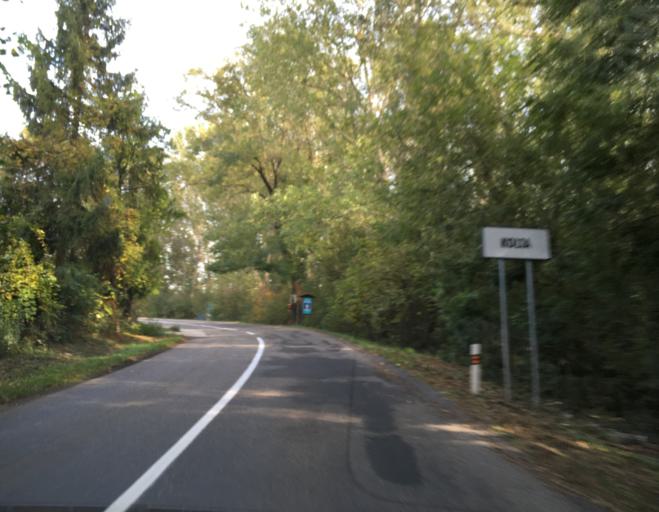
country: SK
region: Nitriansky
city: Svodin
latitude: 48.0054
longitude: 18.4142
